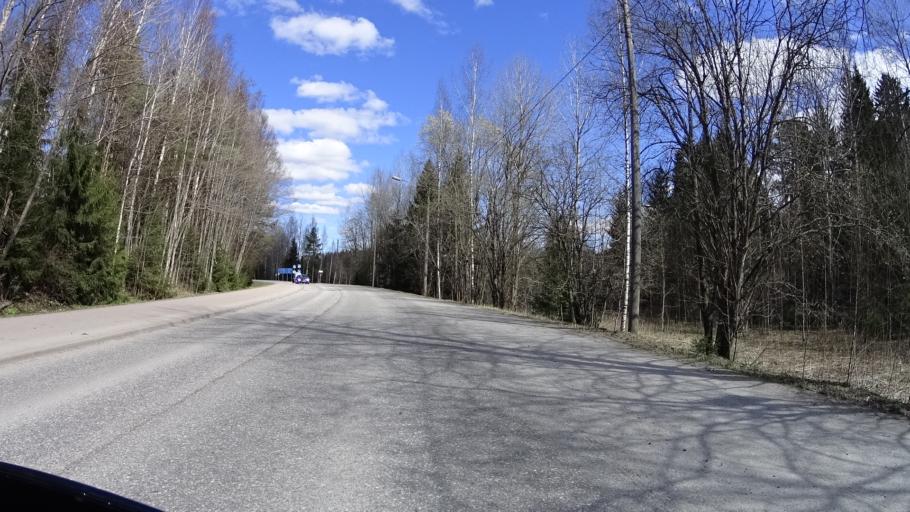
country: FI
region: Uusimaa
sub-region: Helsinki
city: Espoo
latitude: 60.1974
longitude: 24.5975
